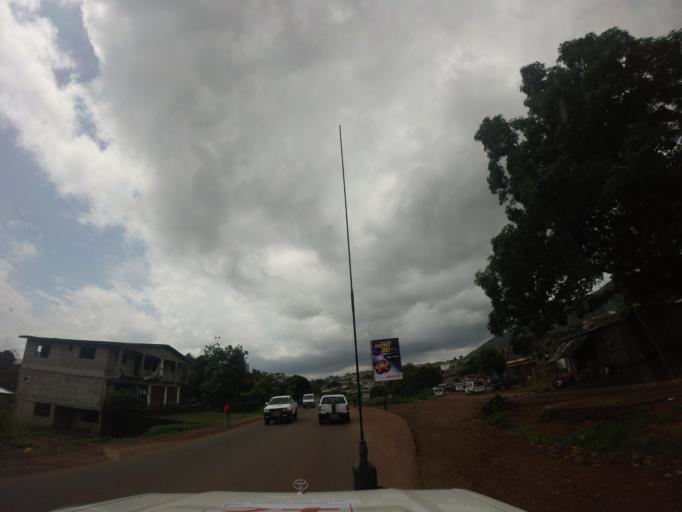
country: SL
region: Western Area
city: Waterloo
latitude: 8.3698
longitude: -13.0929
